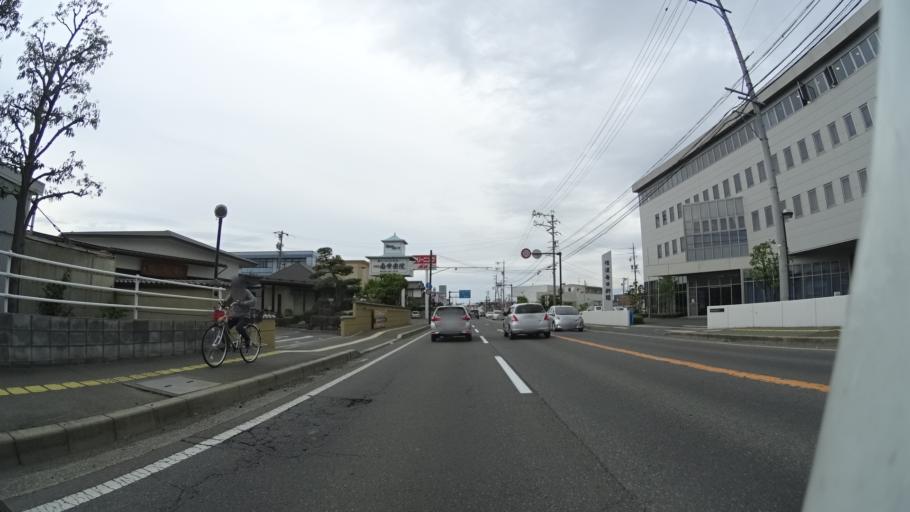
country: JP
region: Nagano
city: Nagano-shi
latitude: 36.6153
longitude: 138.1782
